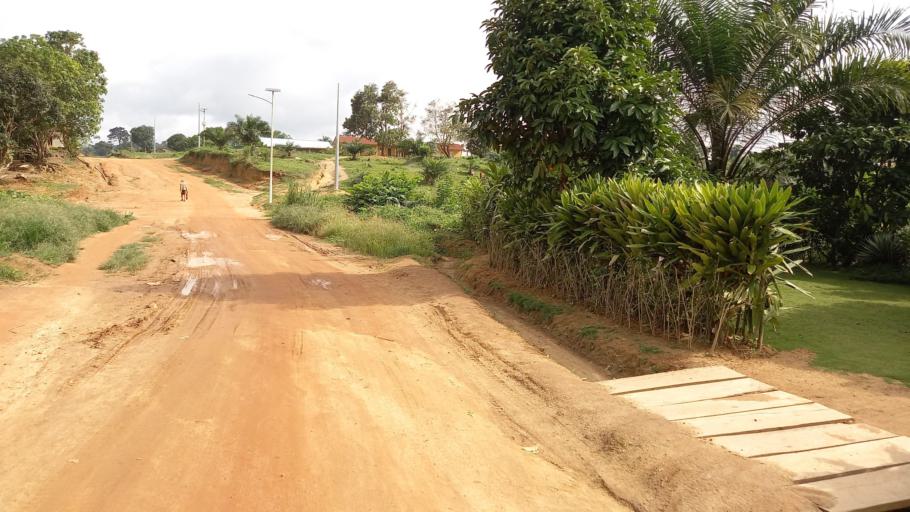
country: SL
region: Eastern Province
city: Kailahun
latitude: 8.2890
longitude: -10.5739
